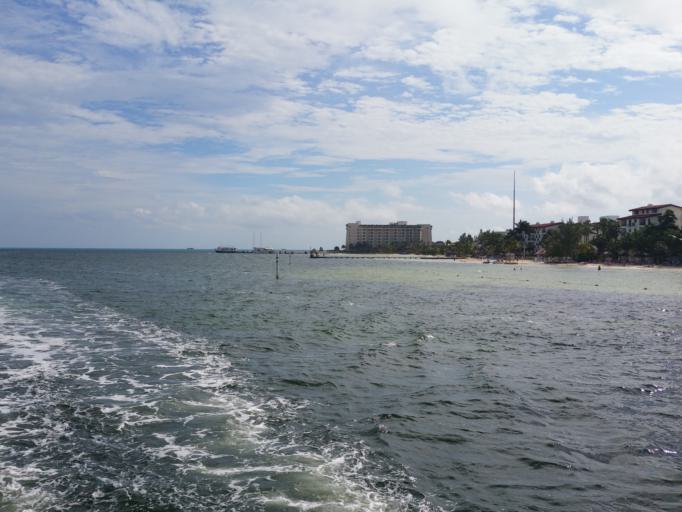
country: MX
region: Quintana Roo
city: Cancun
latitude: 21.1451
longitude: -86.7873
